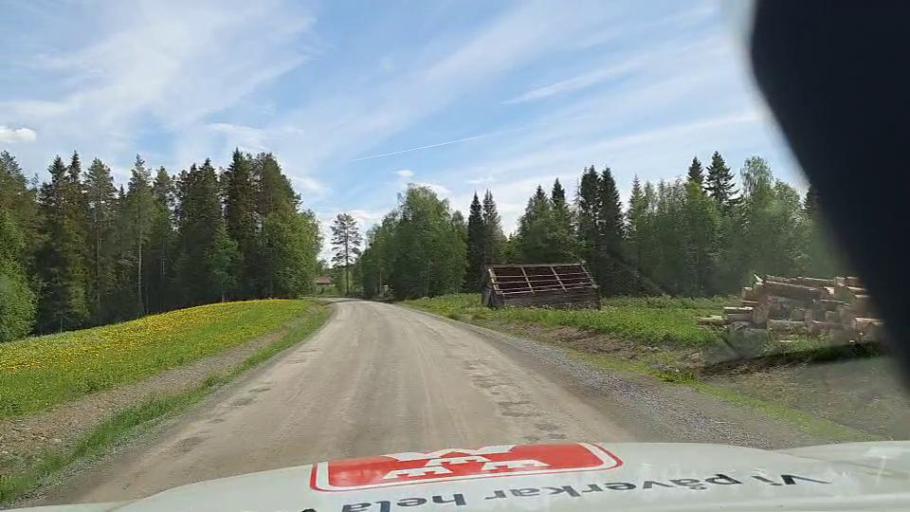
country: SE
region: Jaemtland
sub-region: OEstersunds Kommun
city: Brunflo
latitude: 63.0048
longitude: 14.7936
